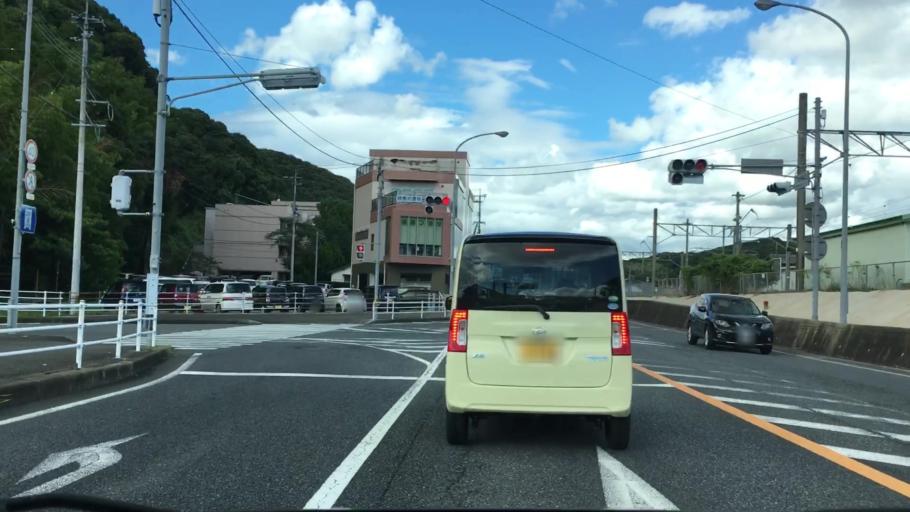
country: JP
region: Nagasaki
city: Sasebo
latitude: 33.1500
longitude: 129.8289
